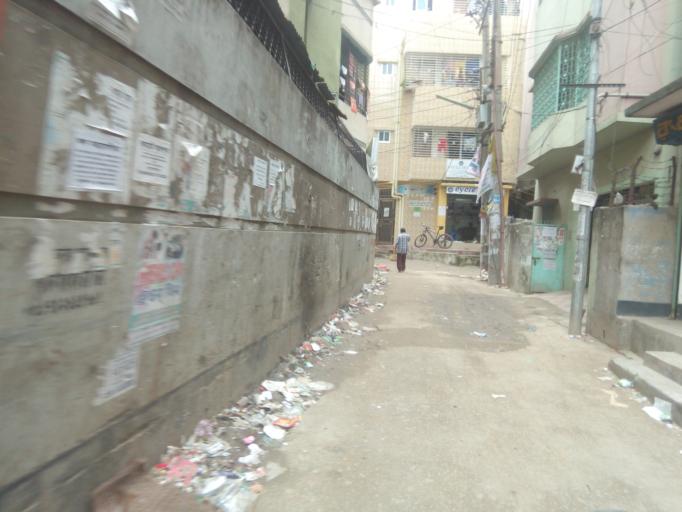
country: BD
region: Dhaka
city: Paltan
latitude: 23.7621
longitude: 90.4208
